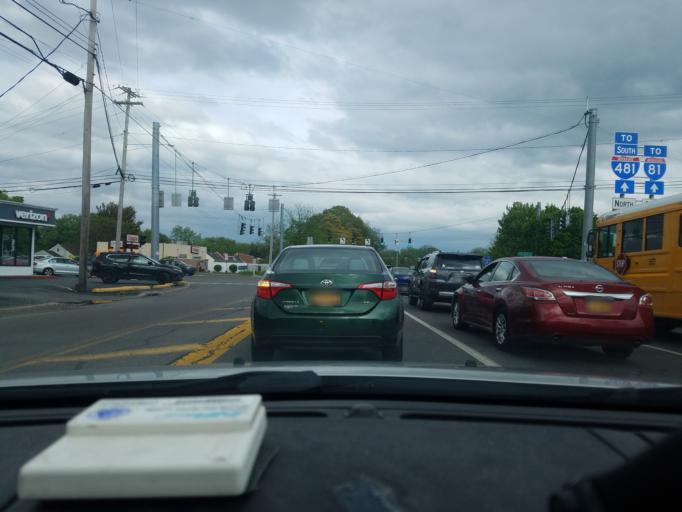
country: US
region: New York
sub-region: Onondaga County
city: North Syracuse
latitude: 43.1450
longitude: -76.1275
